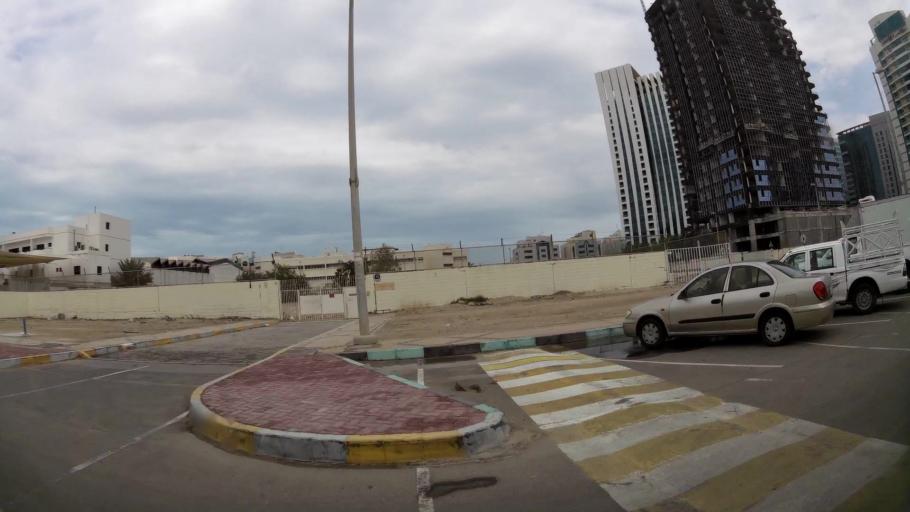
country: AE
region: Abu Dhabi
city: Abu Dhabi
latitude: 24.4304
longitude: 54.4319
